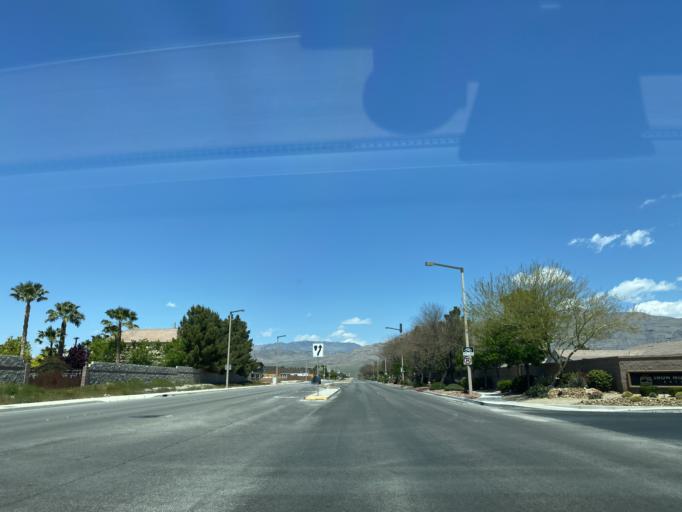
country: US
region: Nevada
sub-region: Clark County
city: North Las Vegas
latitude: 36.3075
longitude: -115.2241
